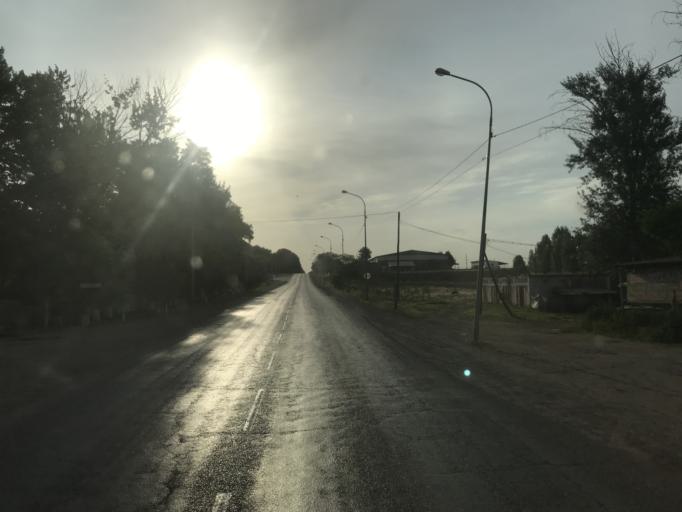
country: KZ
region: Ongtustik Qazaqstan
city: Saryaghash
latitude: 41.4903
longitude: 69.2682
